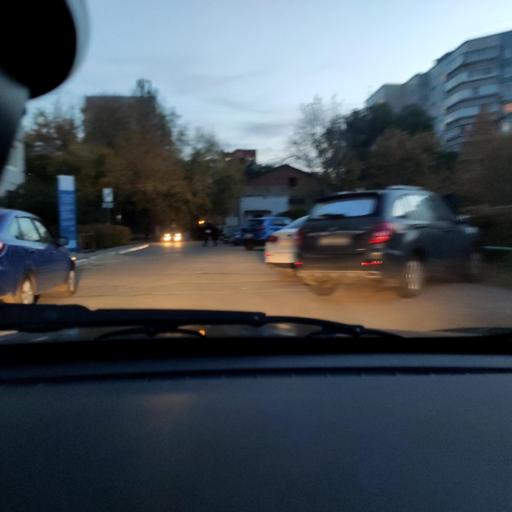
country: RU
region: Samara
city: Tol'yatti
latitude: 53.5478
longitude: 49.3389
